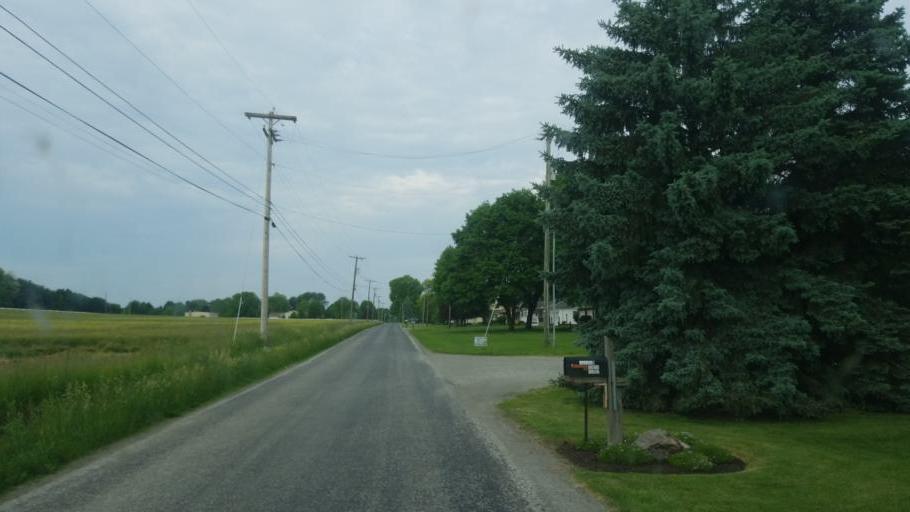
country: US
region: Ohio
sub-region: Wayne County
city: Dalton
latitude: 40.7827
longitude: -81.7487
